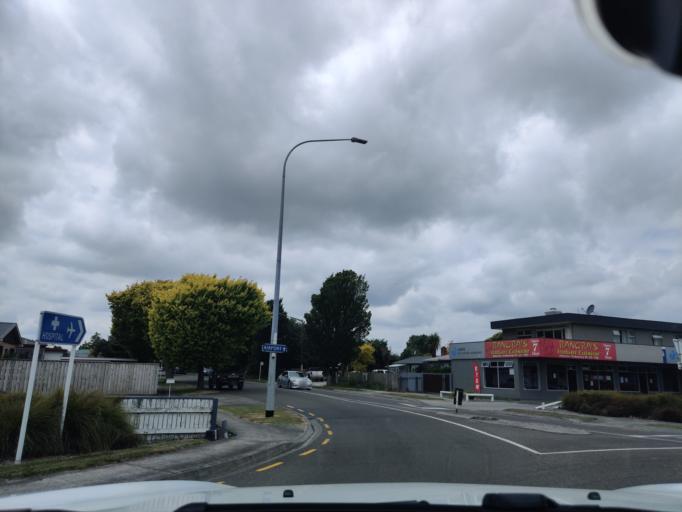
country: NZ
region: Manawatu-Wanganui
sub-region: Palmerston North City
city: Palmerston North
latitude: -40.3508
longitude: 175.5848
